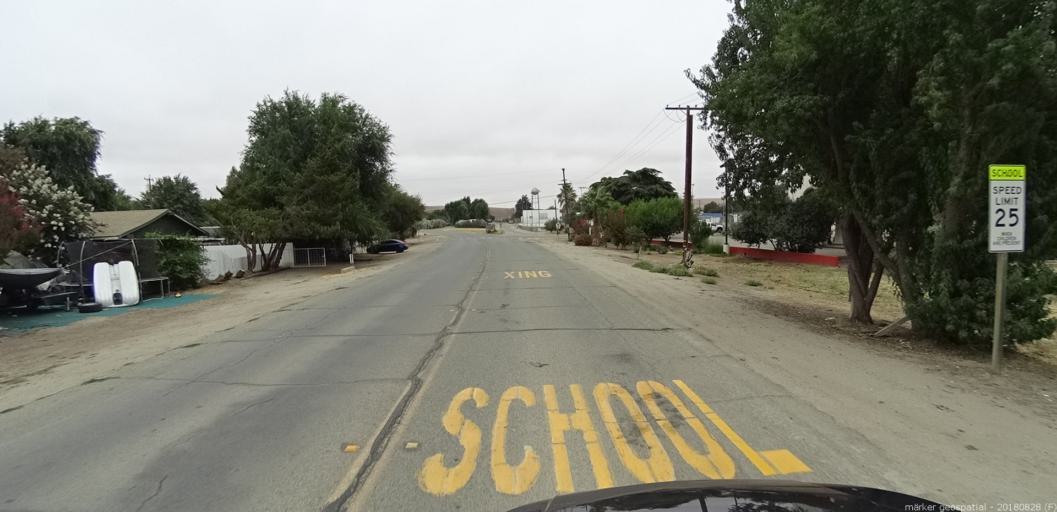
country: US
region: California
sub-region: San Luis Obispo County
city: Lake Nacimiento
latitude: 36.0181
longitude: -120.9082
